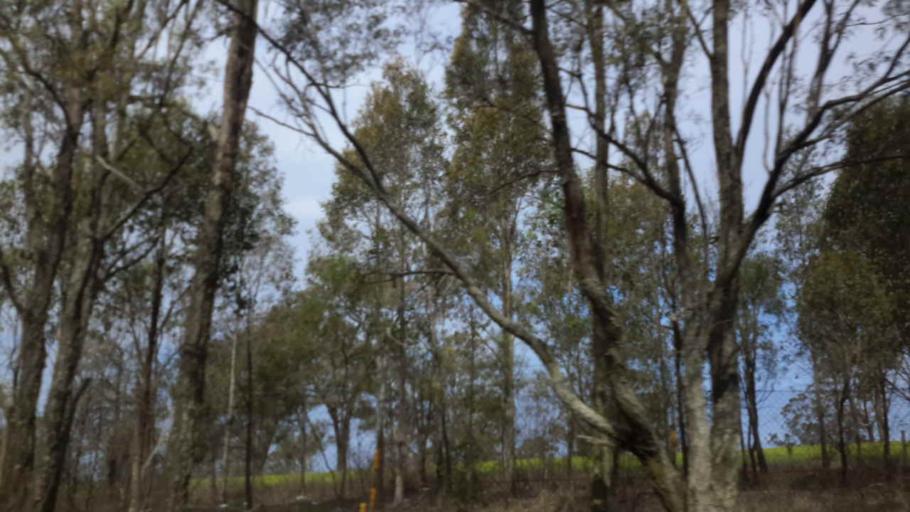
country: AU
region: New South Wales
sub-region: Camden
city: Camden South
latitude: -34.1061
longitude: 150.6986
